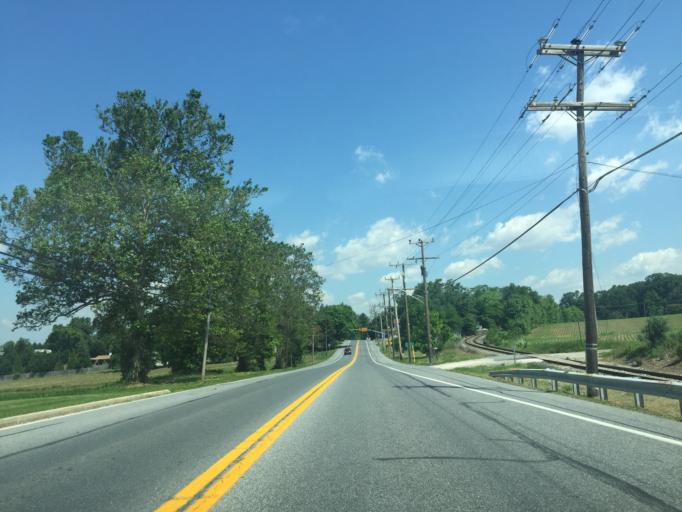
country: US
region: Maryland
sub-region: Baltimore County
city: Reisterstown
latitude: 39.5024
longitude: -76.8332
